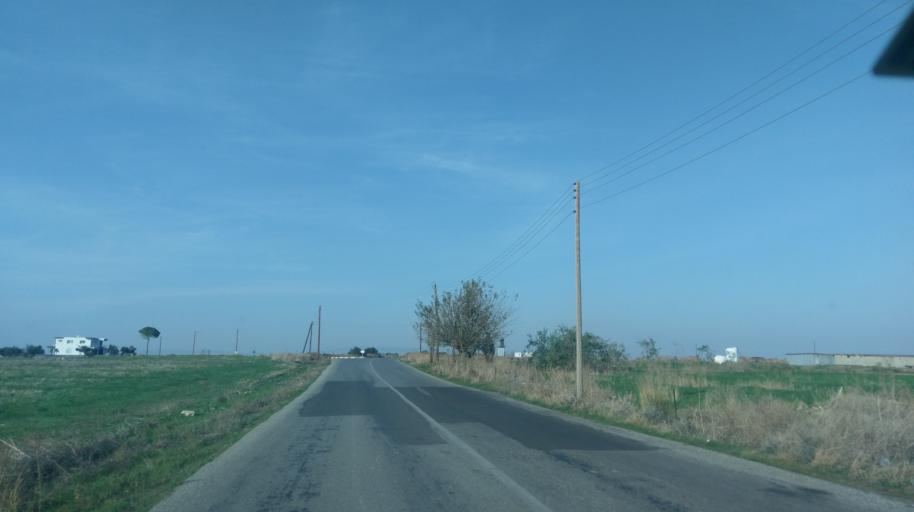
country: CY
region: Larnaka
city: Pergamos
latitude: 35.1132
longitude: 33.7279
